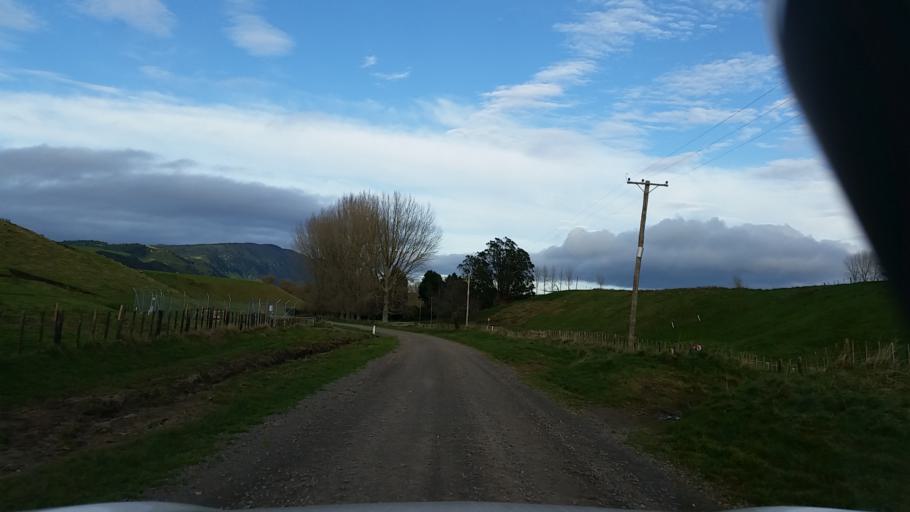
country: NZ
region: Bay of Plenty
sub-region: Rotorua District
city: Rotorua
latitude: -38.3070
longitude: 176.3067
